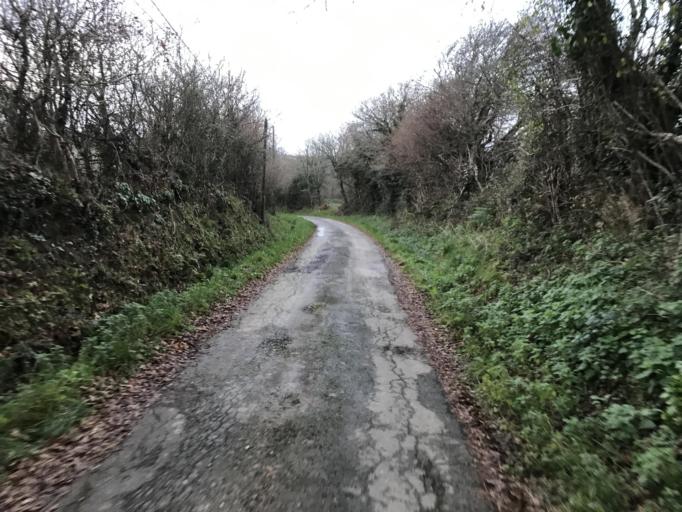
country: FR
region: Brittany
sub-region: Departement du Finistere
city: Loperhet
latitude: 48.3603
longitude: -4.3148
